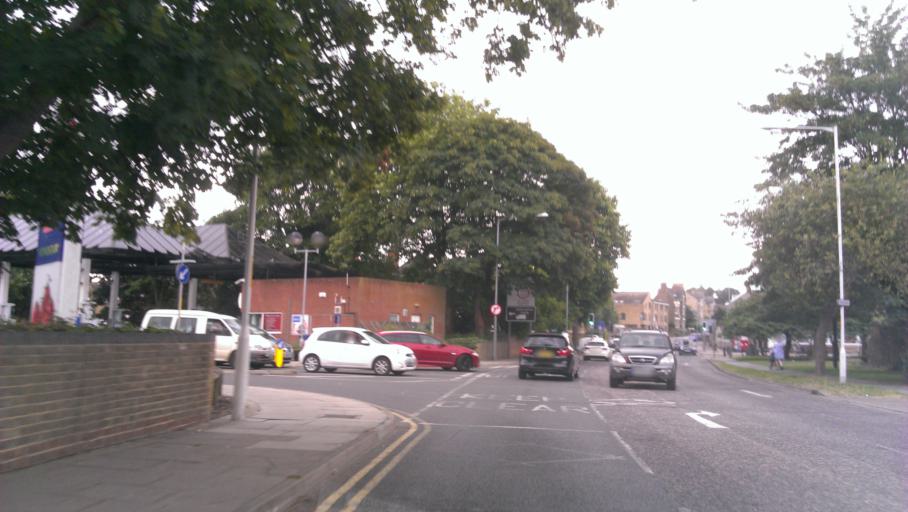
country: GB
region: England
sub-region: Kent
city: Faversham
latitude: 51.3161
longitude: 0.8930
